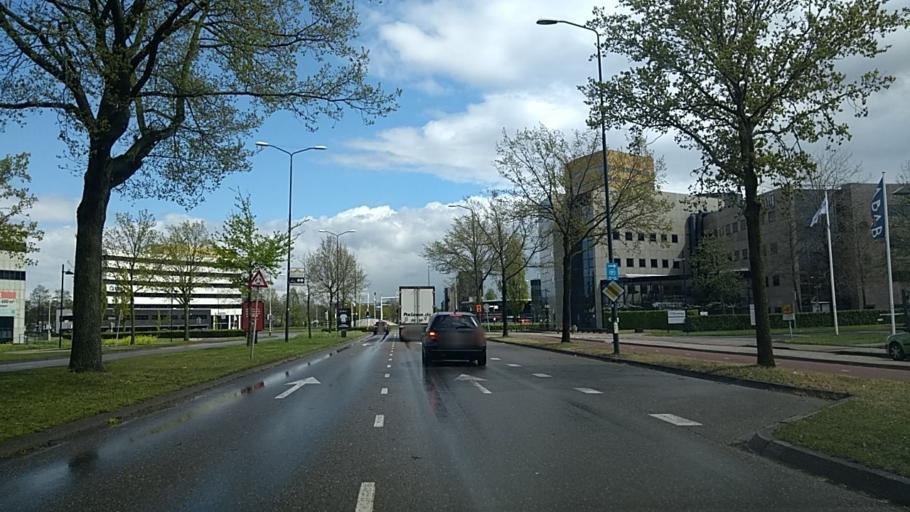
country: NL
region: Gelderland
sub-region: Gemeente Nijmegen
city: Lindenholt
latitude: 51.8245
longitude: 5.7893
